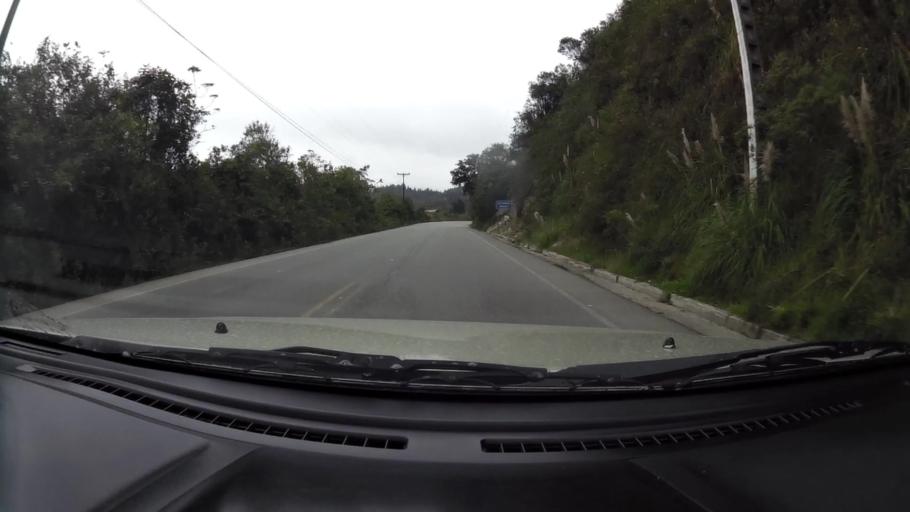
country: EC
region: Canar
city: Canar
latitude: -2.3940
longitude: -78.9849
